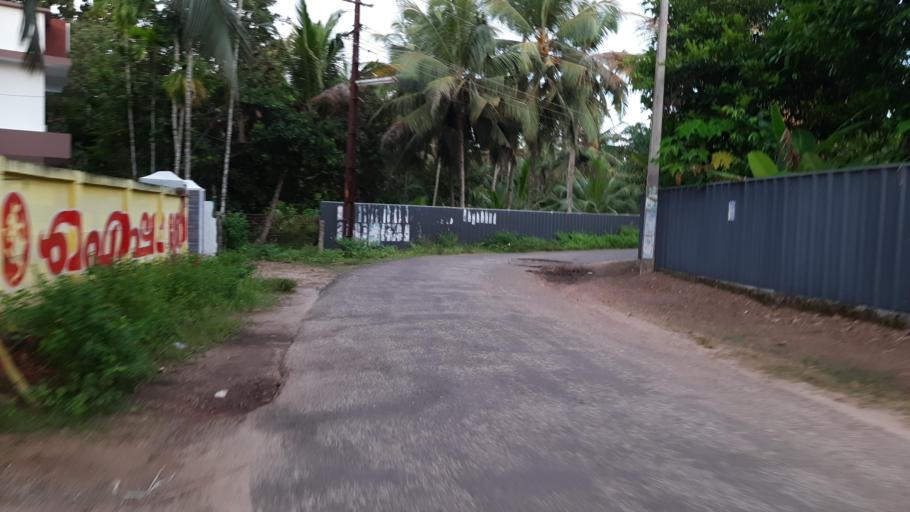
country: IN
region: Kerala
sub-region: Alappuzha
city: Kattanam
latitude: 9.1364
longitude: 76.5448
